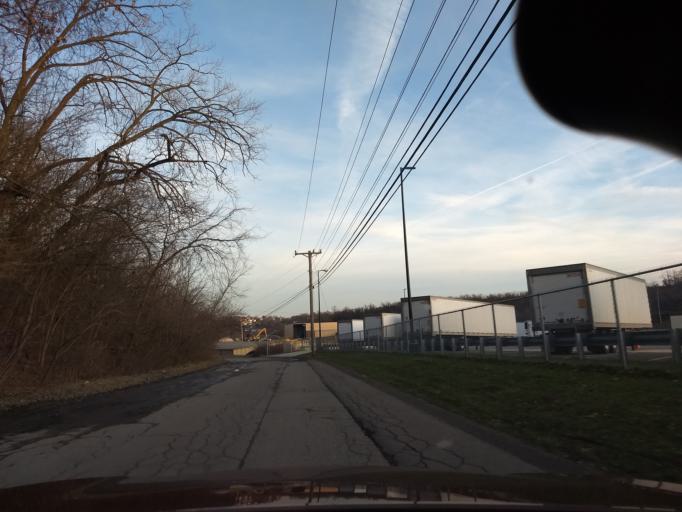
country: US
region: Pennsylvania
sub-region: Allegheny County
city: West Homestead
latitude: 40.3600
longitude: -79.9258
